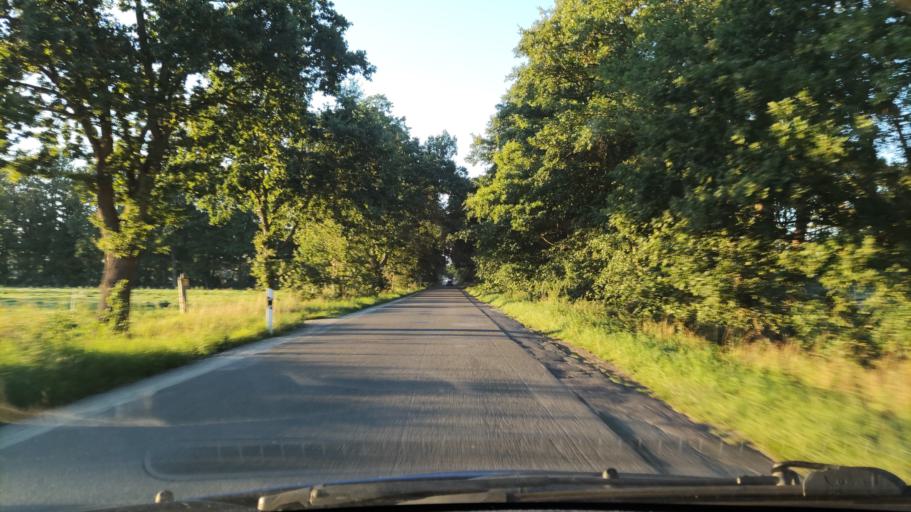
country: DE
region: Lower Saxony
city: Klein Gusborn
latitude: 53.0782
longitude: 11.1933
